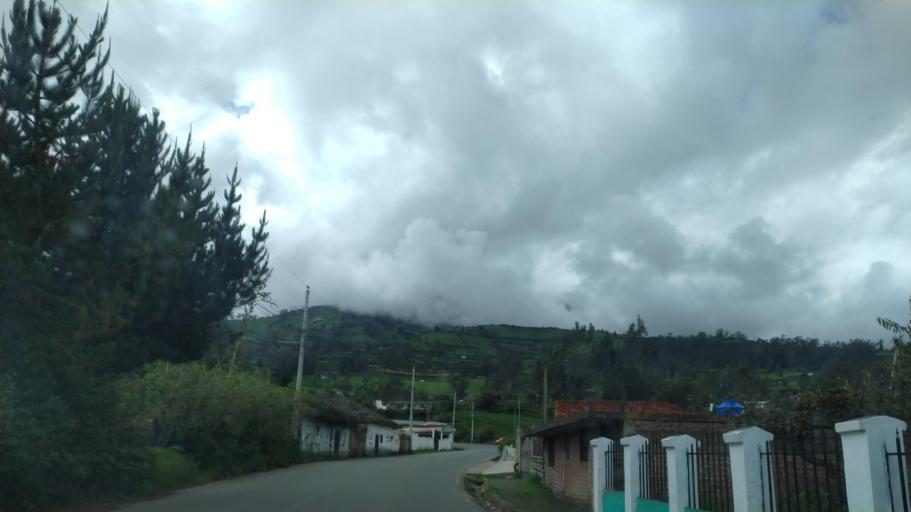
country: EC
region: Chimborazo
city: Riobamba
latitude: -1.6578
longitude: -78.5716
